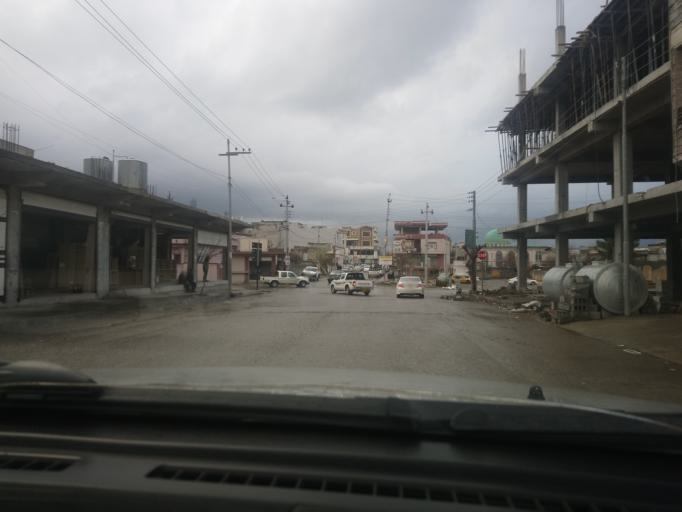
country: IQ
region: As Sulaymaniyah
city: Qeladize
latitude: 36.1846
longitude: 45.1294
